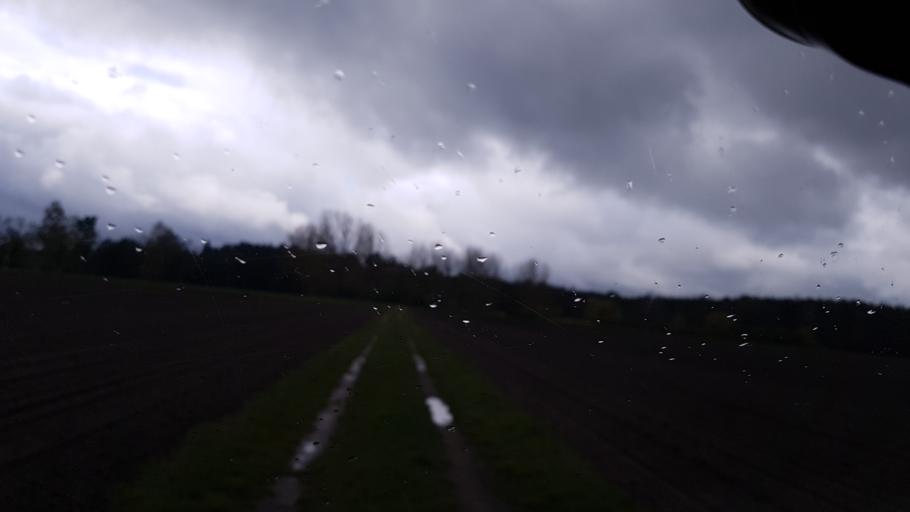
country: DE
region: Brandenburg
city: Doberlug-Kirchhain
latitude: 51.6574
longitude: 13.5189
